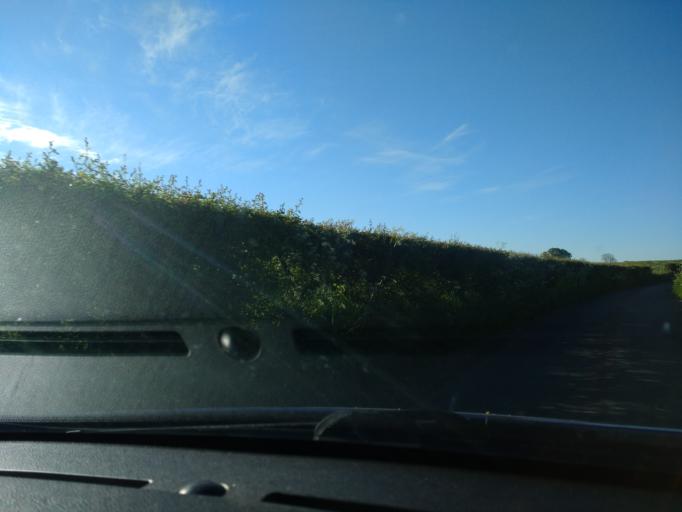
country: GB
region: England
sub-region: Cumbria
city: Appleby-in-Westmorland
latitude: 54.6768
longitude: -2.5901
